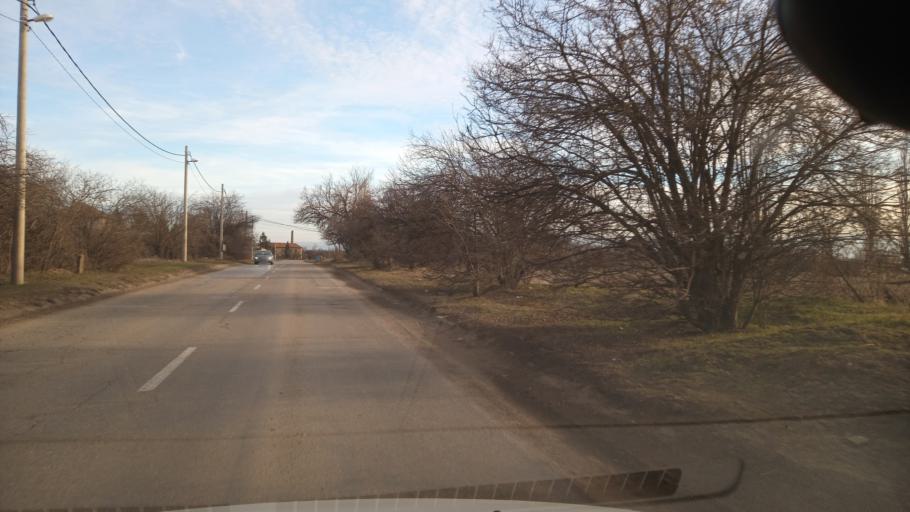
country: BG
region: Sofia-Capital
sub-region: Stolichna Obshtina
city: Bukhovo
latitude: 42.7296
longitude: 23.5537
